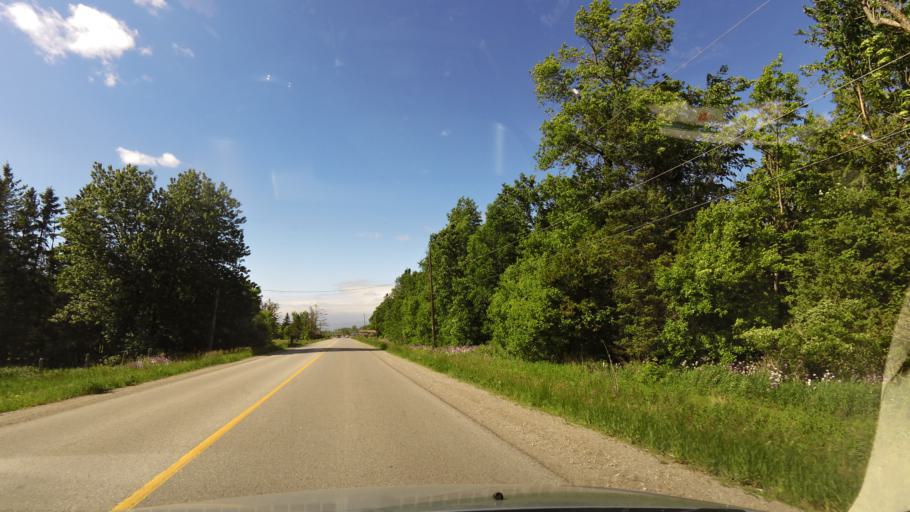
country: CA
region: Ontario
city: Bradford West Gwillimbury
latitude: 44.2022
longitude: -79.6257
